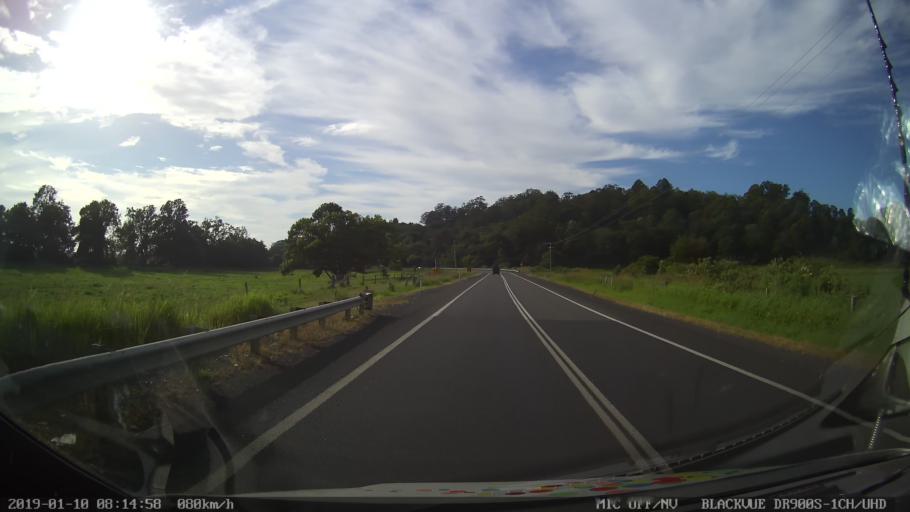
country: AU
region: New South Wales
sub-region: Bellingen
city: Bellingen
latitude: -30.4614
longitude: 152.9188
